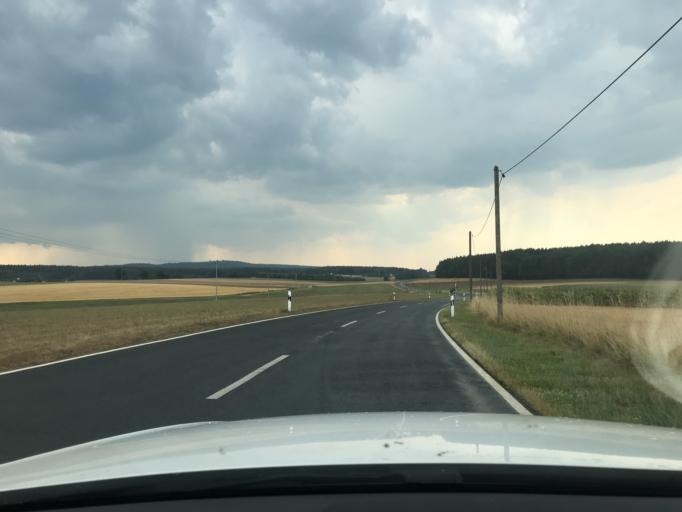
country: DE
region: Bavaria
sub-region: Upper Palatinate
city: Vorbach
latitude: 49.7927
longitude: 11.7611
